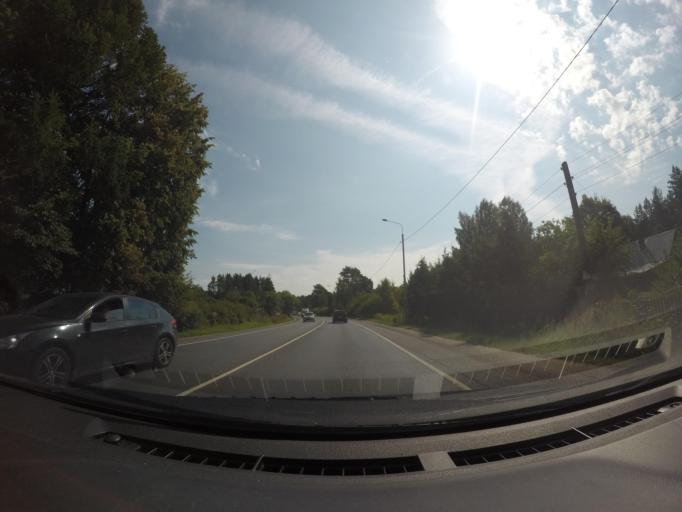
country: RU
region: Moskovskaya
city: Ramenskoye
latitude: 55.6339
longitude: 38.2708
